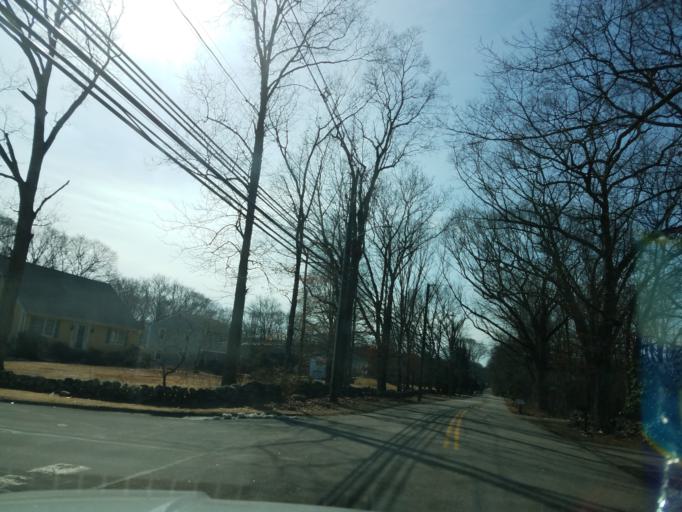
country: US
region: Connecticut
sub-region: New London County
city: Pawcatuck
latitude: 41.3992
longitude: -71.8539
